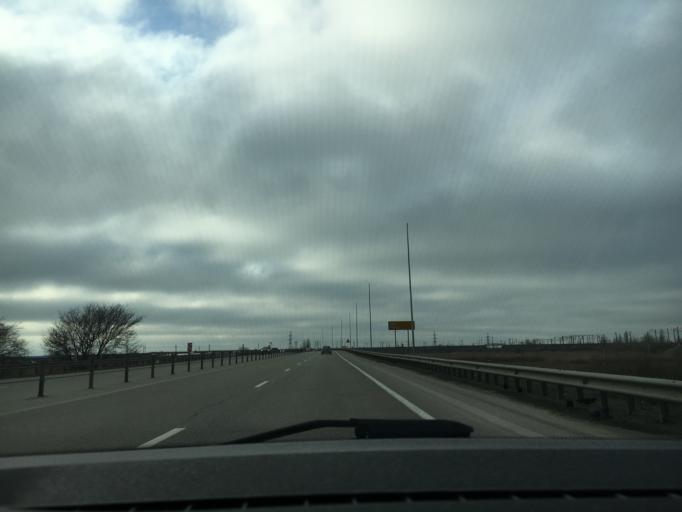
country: RU
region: Rostov
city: Bataysk
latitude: 47.1492
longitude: 39.7078
